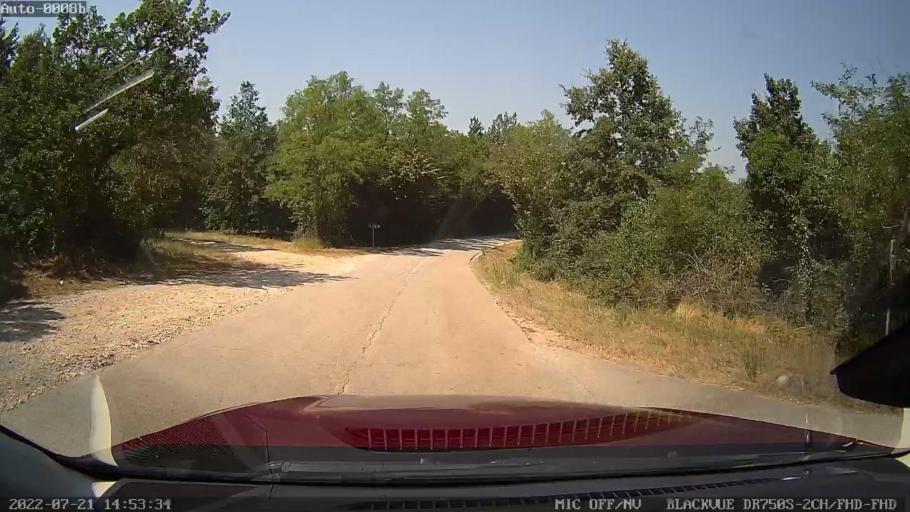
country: HR
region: Istarska
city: Pazin
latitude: 45.1828
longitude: 13.9318
